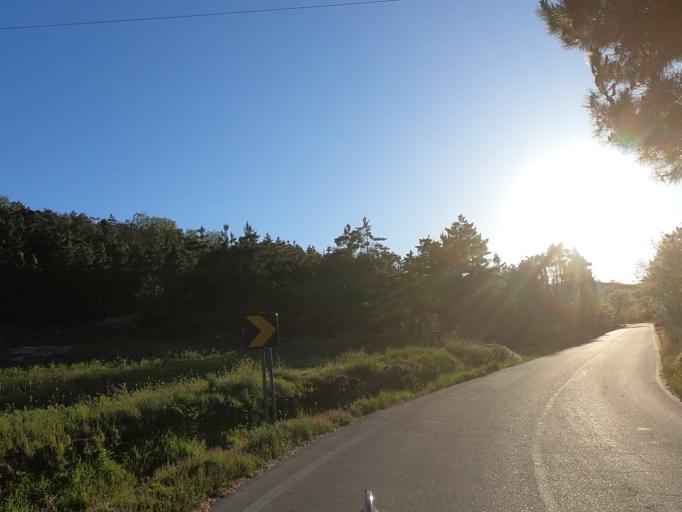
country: PT
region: Vila Real
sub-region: Sabrosa
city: Sabrosa
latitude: 41.3571
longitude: -7.6272
